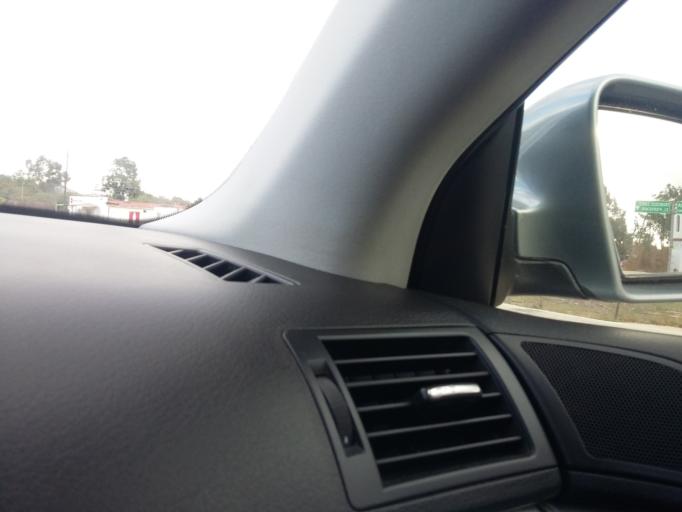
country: MX
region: Baja California
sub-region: Ensenada
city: Rancho Verde
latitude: 32.1017
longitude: -116.5630
